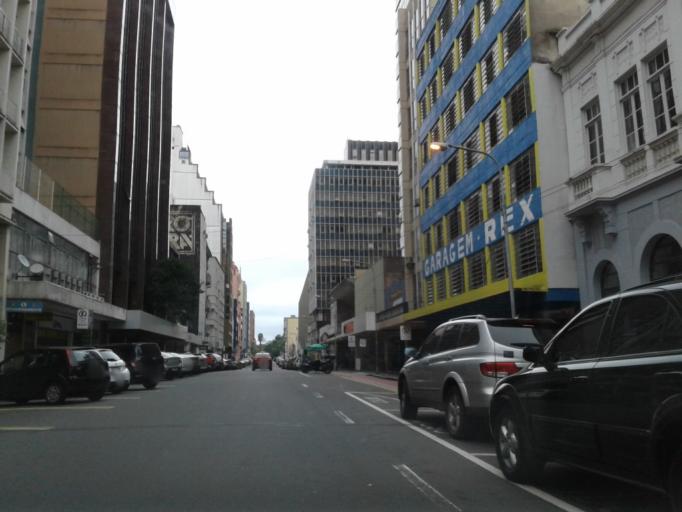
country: BR
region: Rio Grande do Sul
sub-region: Porto Alegre
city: Porto Alegre
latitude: -30.0300
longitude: -51.2325
